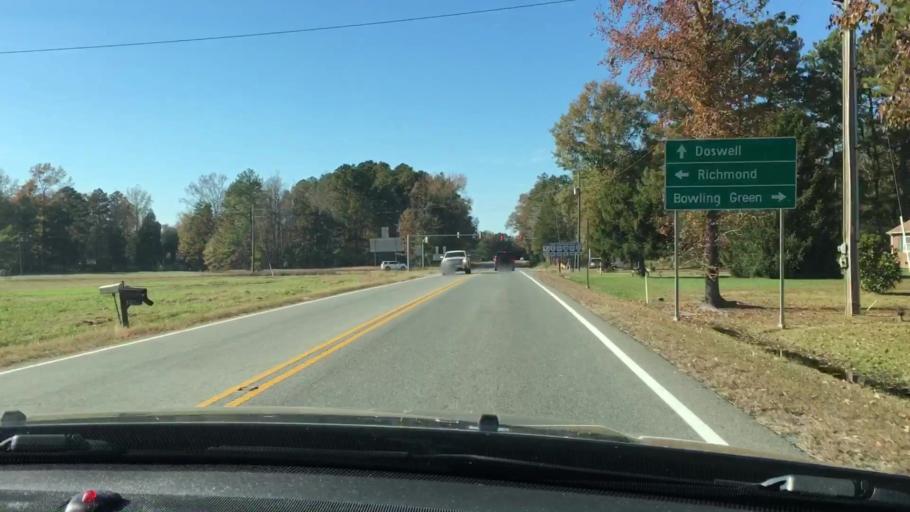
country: US
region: Virginia
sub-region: Hanover County
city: Hanover
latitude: 37.8340
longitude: -77.3676
